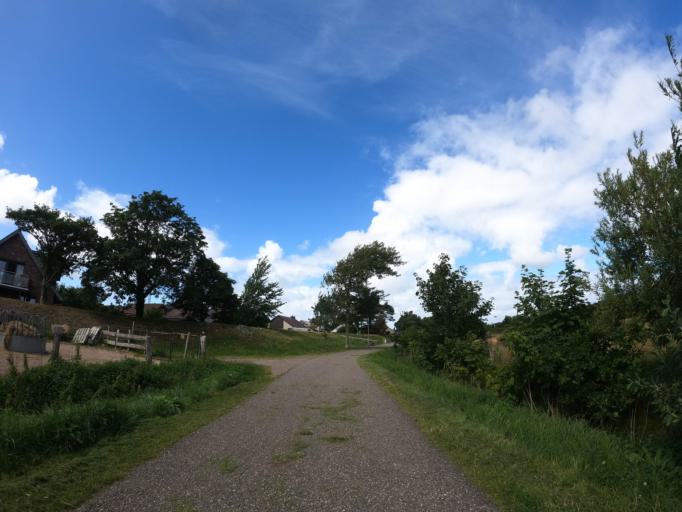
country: DE
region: Schleswig-Holstein
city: Westerland
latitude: 54.8965
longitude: 8.3141
